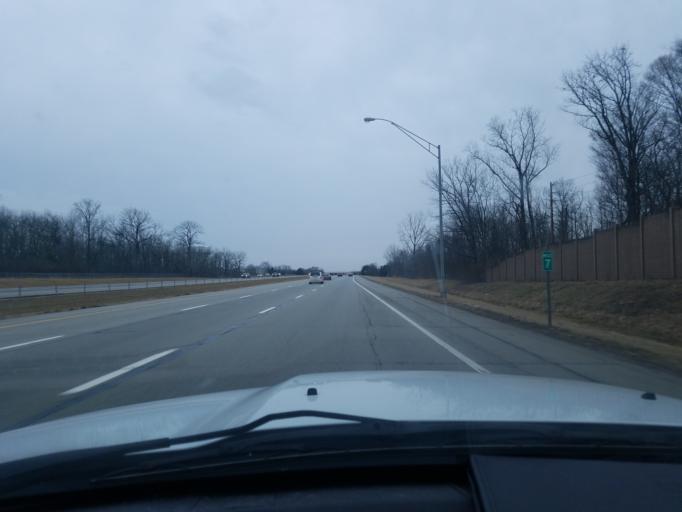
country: US
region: Ohio
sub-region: Montgomery County
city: Centerville
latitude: 39.6552
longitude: -84.1177
